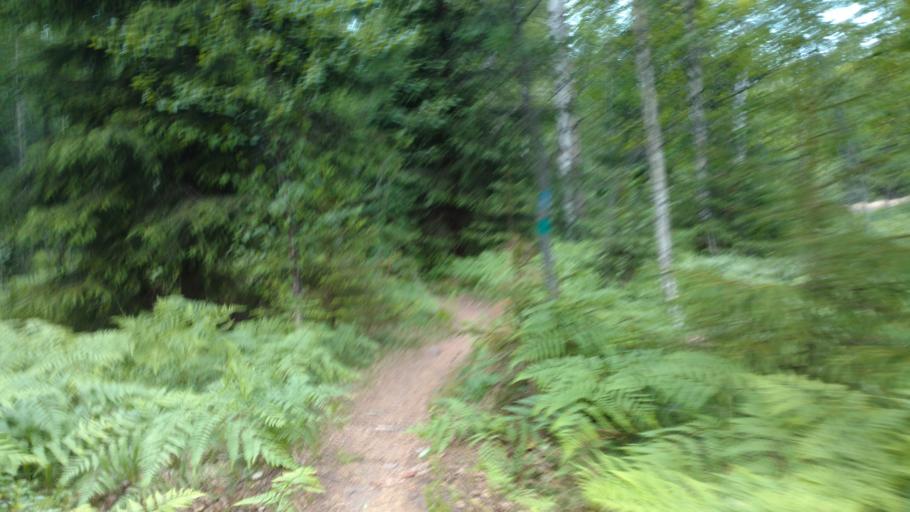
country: FI
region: Uusimaa
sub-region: Raaseporin
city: Pohja
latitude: 60.1171
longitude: 23.5480
